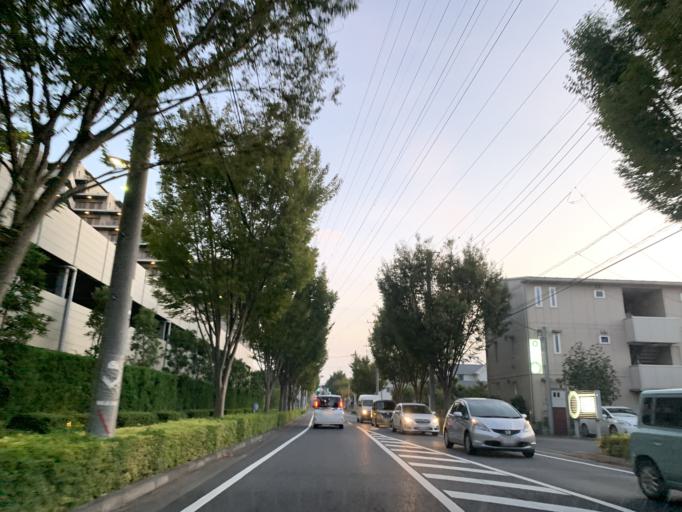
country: JP
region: Chiba
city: Nagareyama
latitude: 35.8766
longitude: 139.9337
